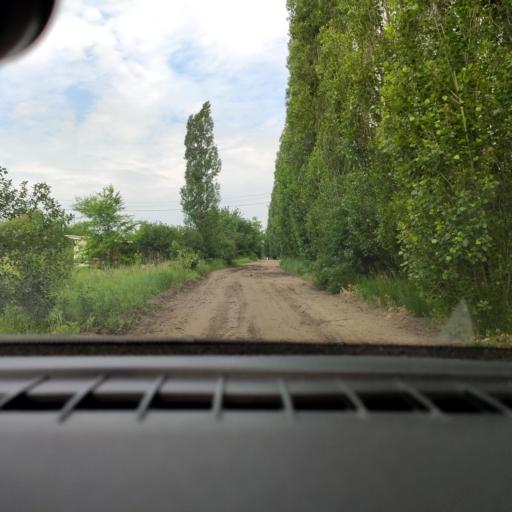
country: RU
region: Voronezj
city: Maslovka
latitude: 51.5016
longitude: 39.1957
